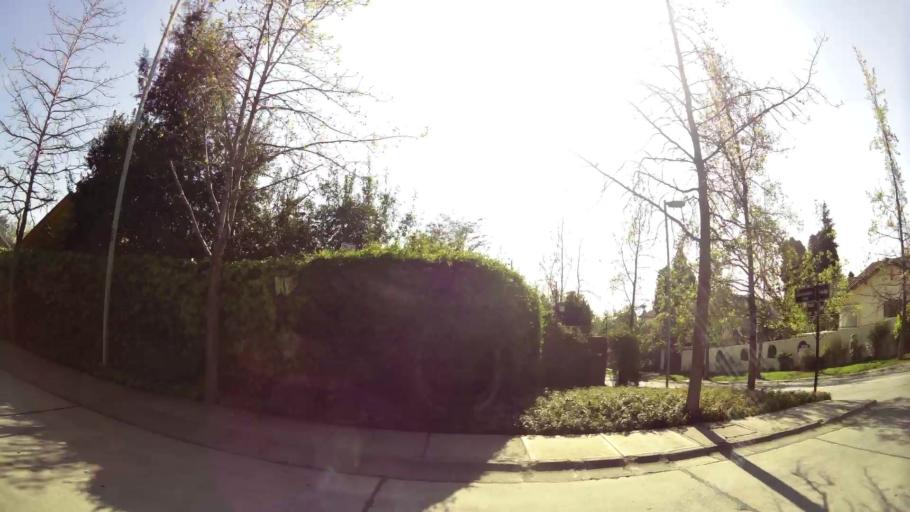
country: CL
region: Santiago Metropolitan
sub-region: Provincia de Santiago
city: Villa Presidente Frei, Nunoa, Santiago, Chile
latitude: -33.3698
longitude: -70.4984
